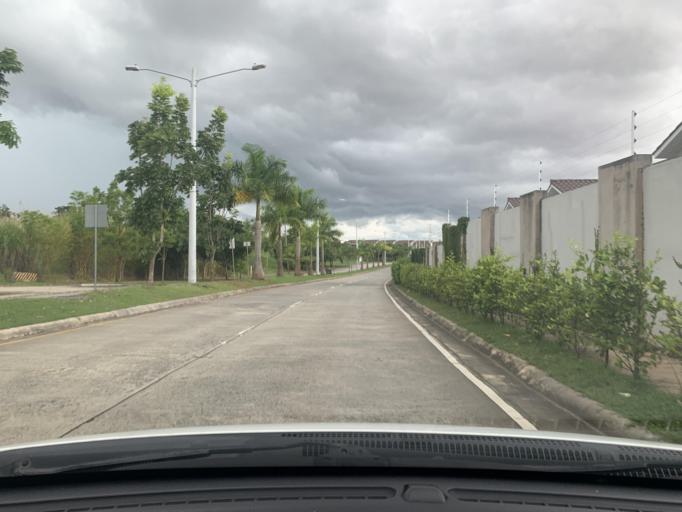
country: PA
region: Panama
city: San Miguelito
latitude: 9.0887
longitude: -79.4646
